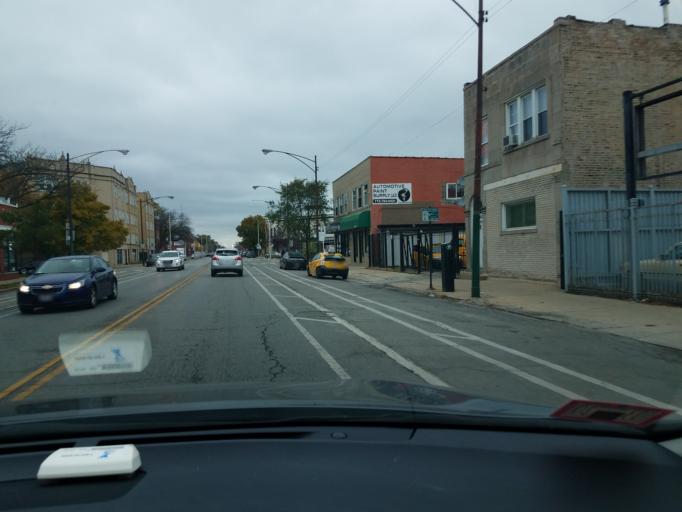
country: US
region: Illinois
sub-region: Cook County
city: Lincolnwood
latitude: 41.9567
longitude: -87.7234
